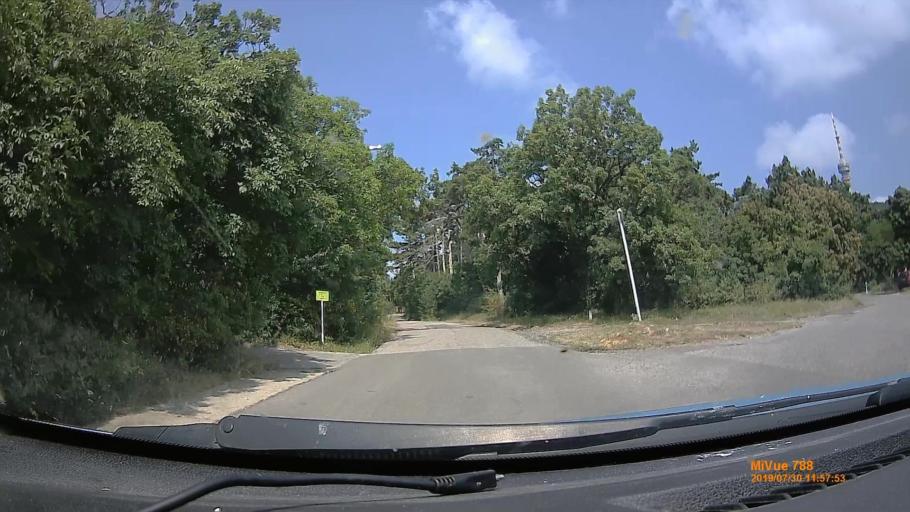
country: HU
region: Baranya
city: Pecs
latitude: 46.0896
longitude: 18.2157
